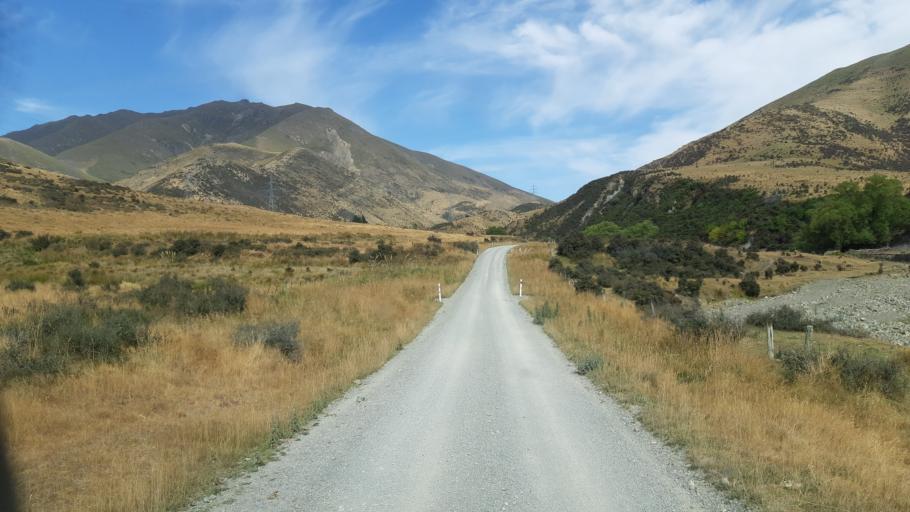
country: NZ
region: Canterbury
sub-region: Timaru District
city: Pleasant Point
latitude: -44.1893
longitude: 170.6530
